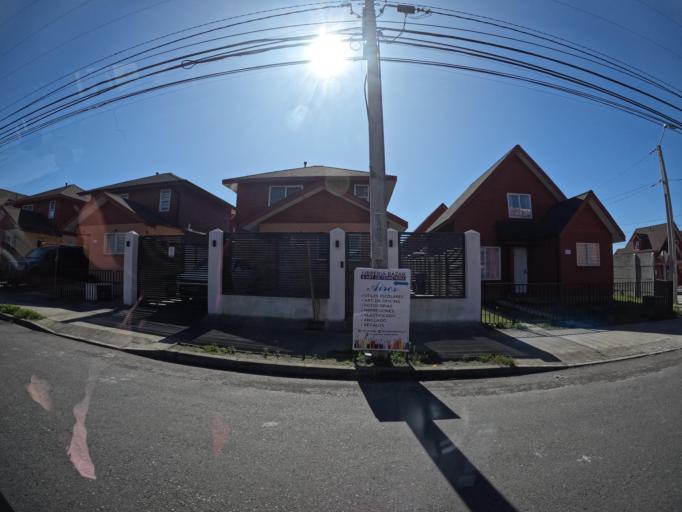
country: CL
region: Biobio
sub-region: Provincia de Concepcion
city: Concepcion
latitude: -36.8820
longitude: -73.1474
